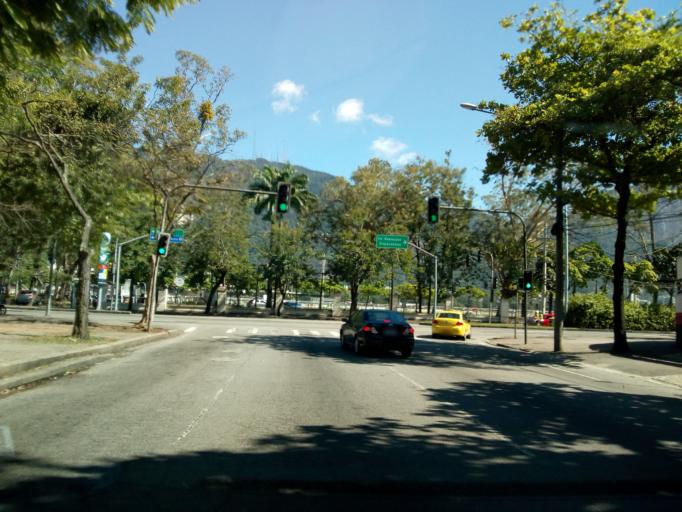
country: BR
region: Rio de Janeiro
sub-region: Rio De Janeiro
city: Rio de Janeiro
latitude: -22.9781
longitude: -43.2221
